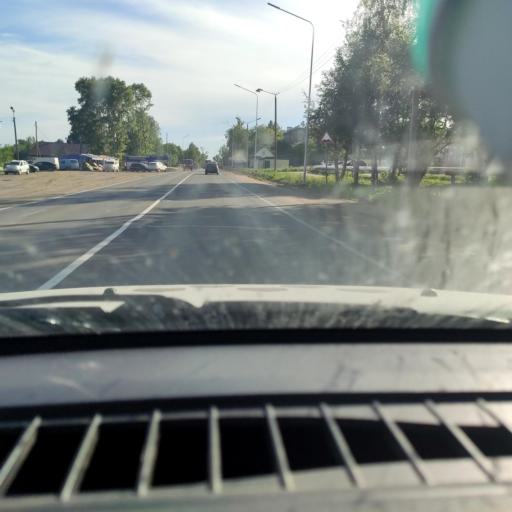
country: RU
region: Kirov
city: Vakhrushi
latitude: 58.6837
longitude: 50.0341
